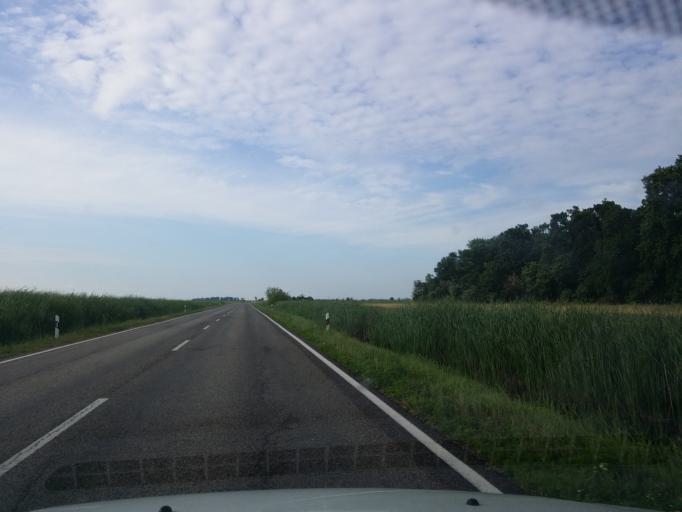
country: HU
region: Hajdu-Bihar
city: Egyek
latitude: 47.5636
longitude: 20.8626
